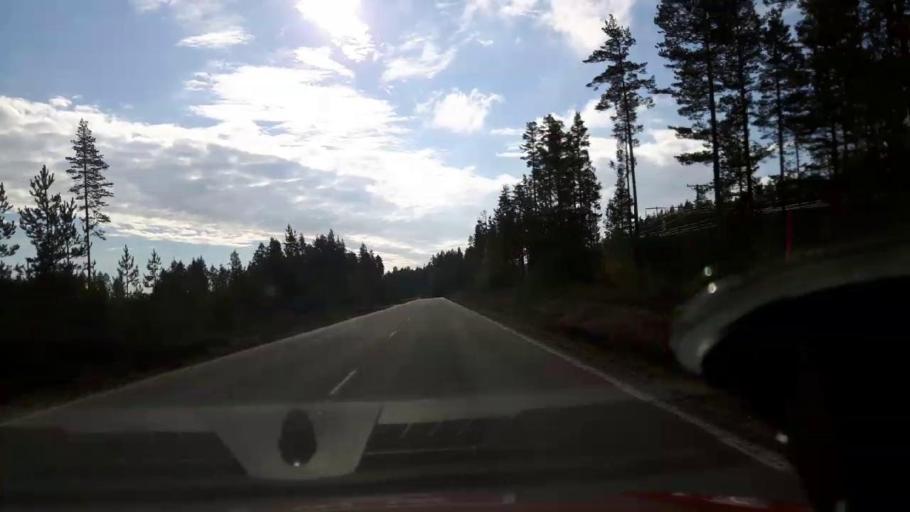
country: SE
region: Vaesternorrland
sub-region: Ange Kommun
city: Ange
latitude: 62.0630
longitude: 15.1120
